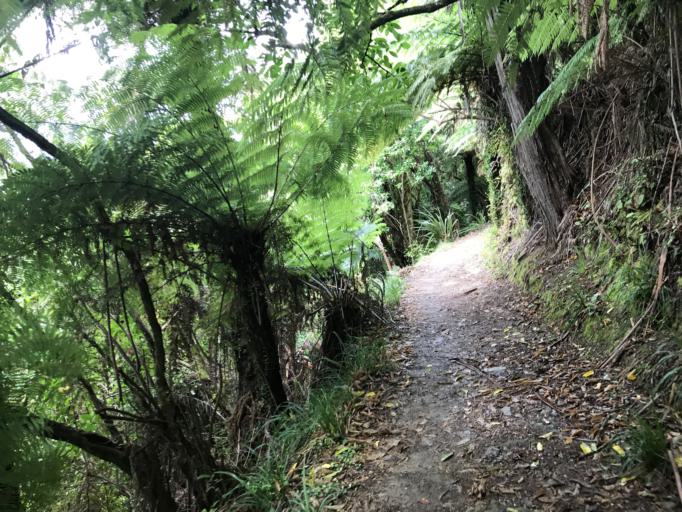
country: NZ
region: Marlborough
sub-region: Marlborough District
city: Picton
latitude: -41.2512
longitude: 173.9526
